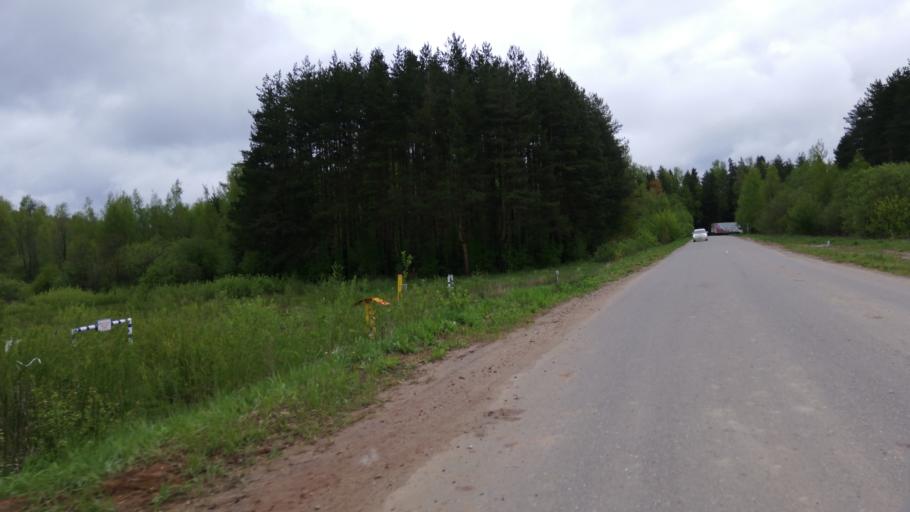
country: RU
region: Ivanovo
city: Novo-Talitsy
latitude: 57.0201
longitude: 40.7696
